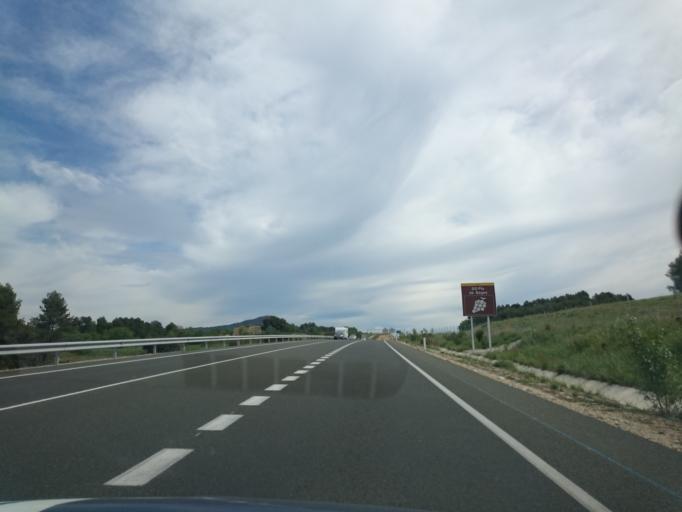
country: ES
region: Catalonia
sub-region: Provincia de Barcelona
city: Castelloli
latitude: 41.6217
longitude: 1.6838
